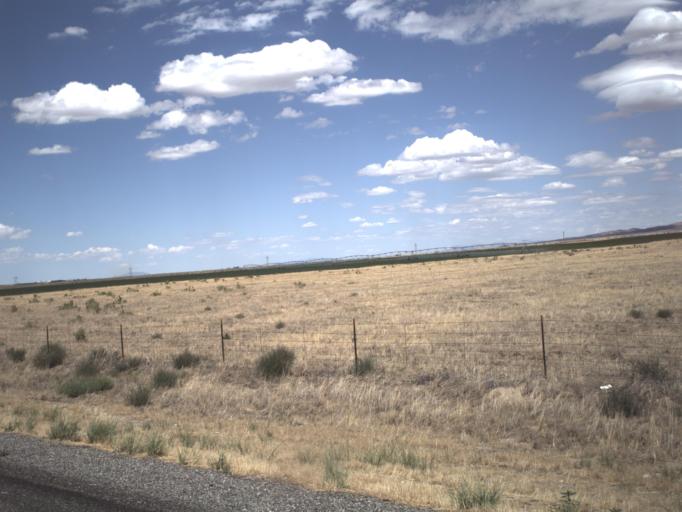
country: US
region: Utah
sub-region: Millard County
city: Fillmore
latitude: 39.1391
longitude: -112.3715
